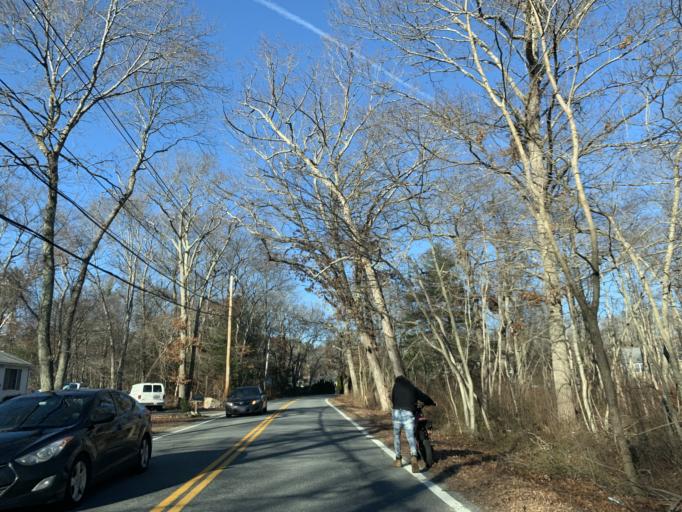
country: US
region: Rhode Island
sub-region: Washington County
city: Exeter
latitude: 41.5674
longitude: -71.5367
